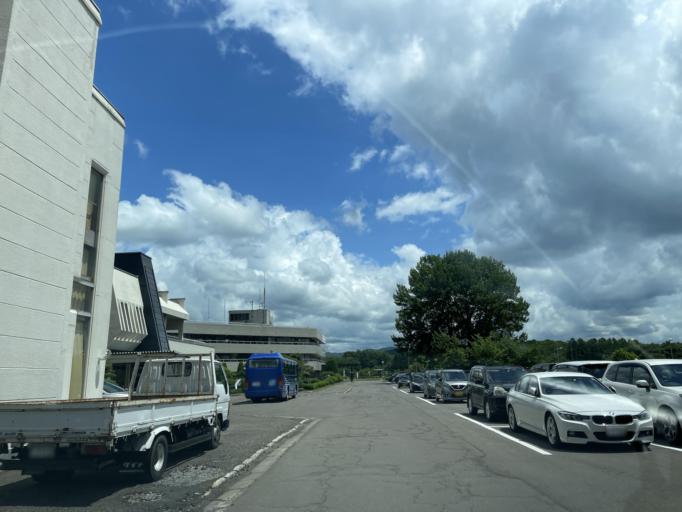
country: JP
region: Iwate
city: Ichinohe
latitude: 39.9724
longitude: 141.2113
